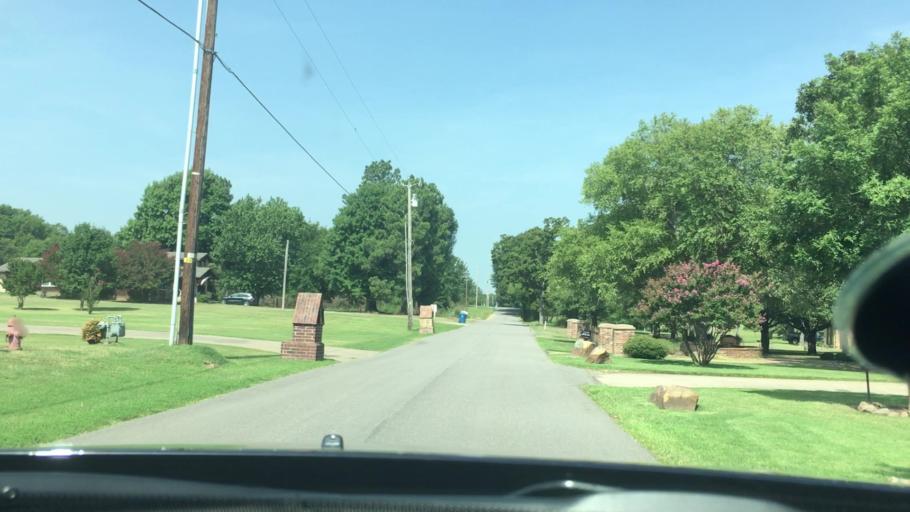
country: US
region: Oklahoma
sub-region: Atoka County
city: Atoka
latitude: 34.3603
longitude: -96.1482
